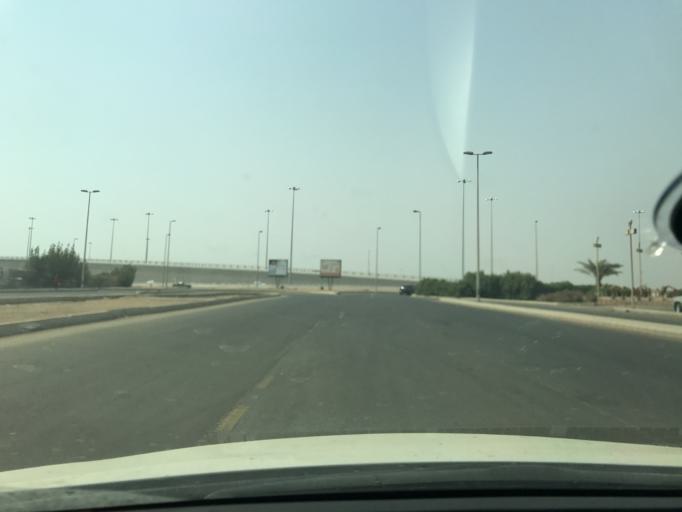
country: SA
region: Makkah
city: Jeddah
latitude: 21.6328
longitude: 39.1605
